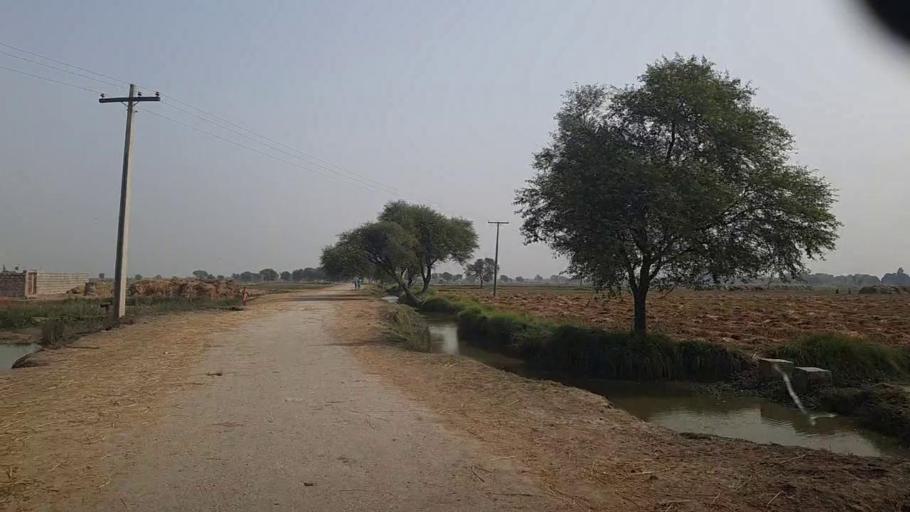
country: PK
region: Sindh
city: Kashmor
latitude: 28.3796
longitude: 69.4386
